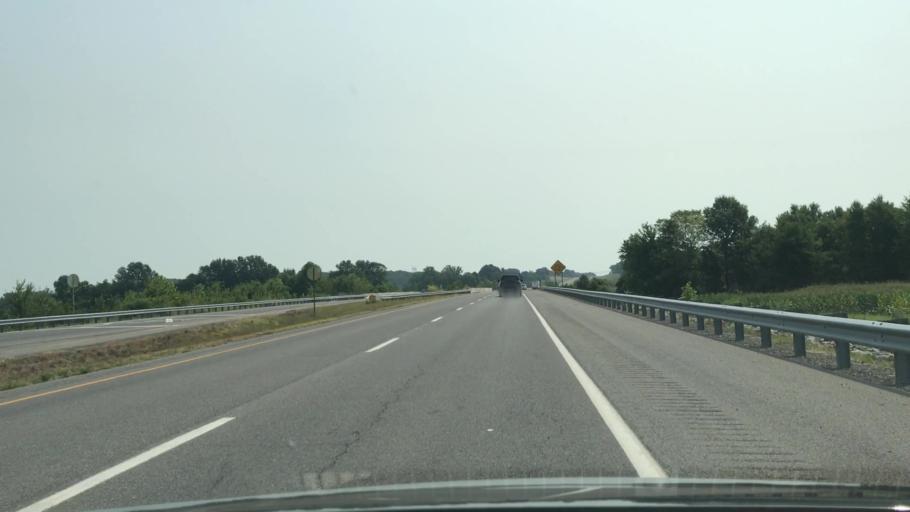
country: US
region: Kentucky
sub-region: Calloway County
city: Murray
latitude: 36.6517
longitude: -88.2902
